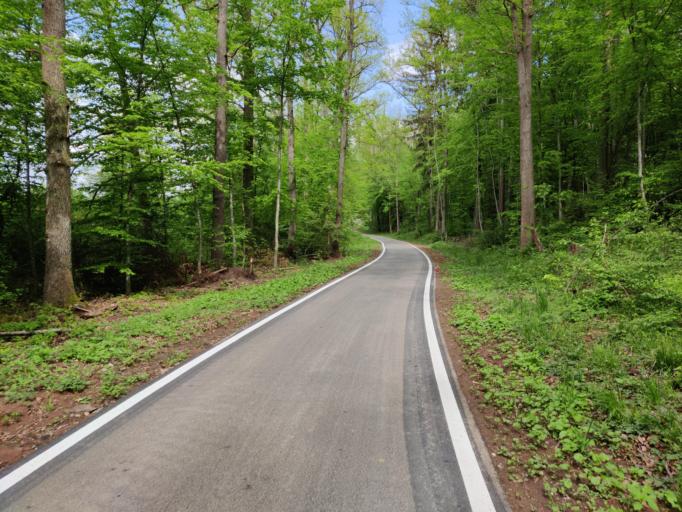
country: DE
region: Baden-Wuerttemberg
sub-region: Tuebingen Region
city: Tuebingen
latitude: 48.4939
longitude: 9.0669
